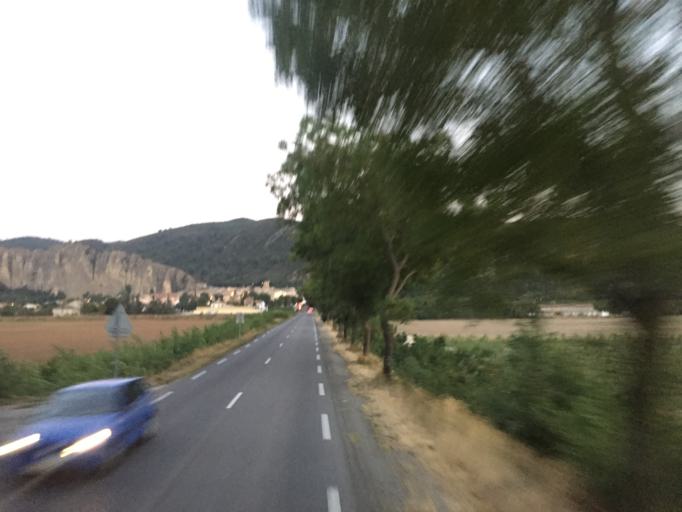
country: FR
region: Provence-Alpes-Cote d'Azur
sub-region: Departement des Alpes-de-Haute-Provence
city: Les Mees
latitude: 44.0343
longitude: 5.9668
